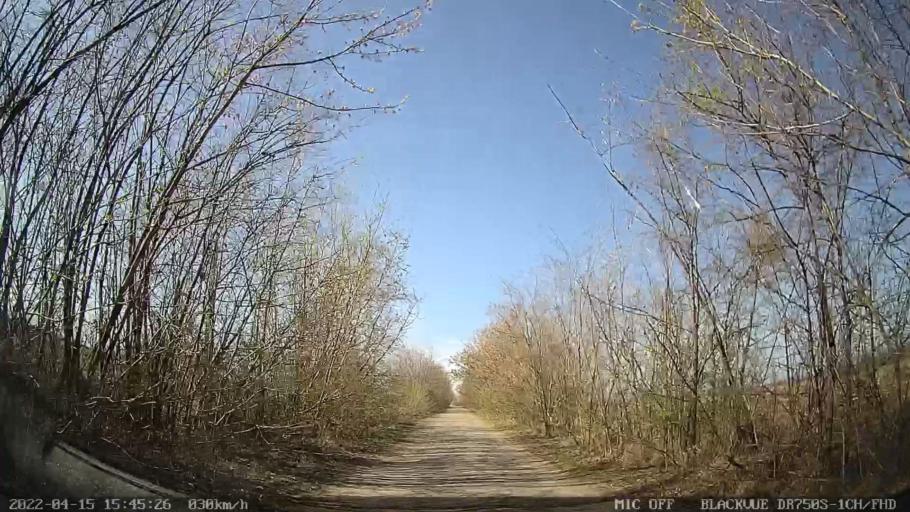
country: MD
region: Raionul Ocnita
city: Otaci
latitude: 48.3763
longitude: 27.9183
